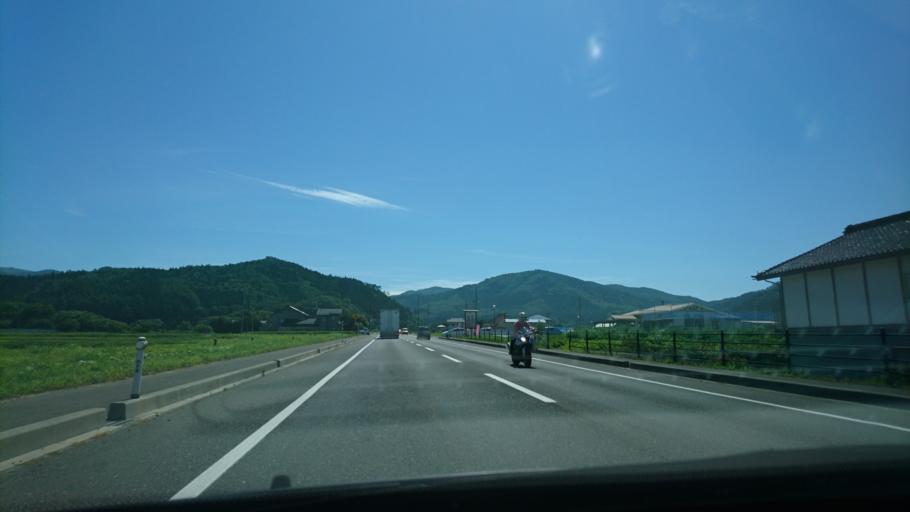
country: JP
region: Iwate
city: Tono
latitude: 39.2726
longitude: 141.5821
